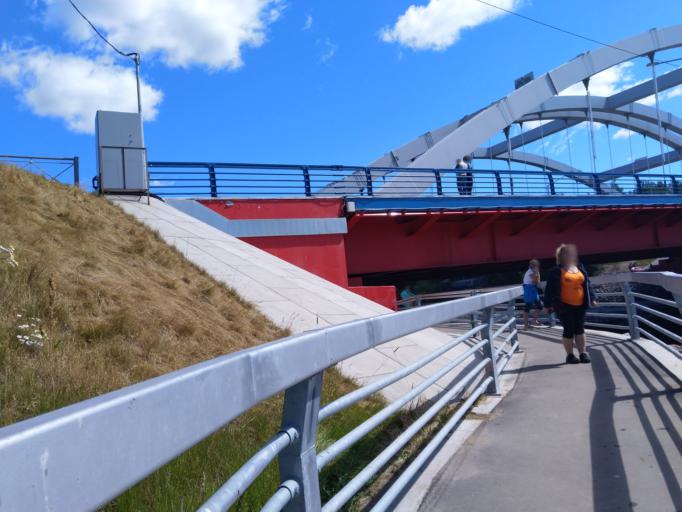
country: RU
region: Leningrad
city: Sapernoye
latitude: 60.6802
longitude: 30.0046
